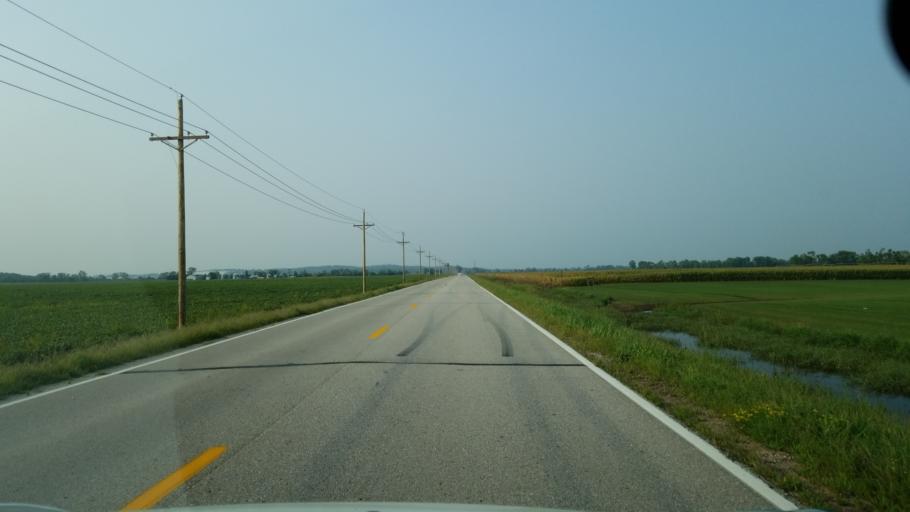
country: US
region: Nebraska
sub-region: Sarpy County
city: Offutt Air Force Base
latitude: 41.0849
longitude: -95.8899
